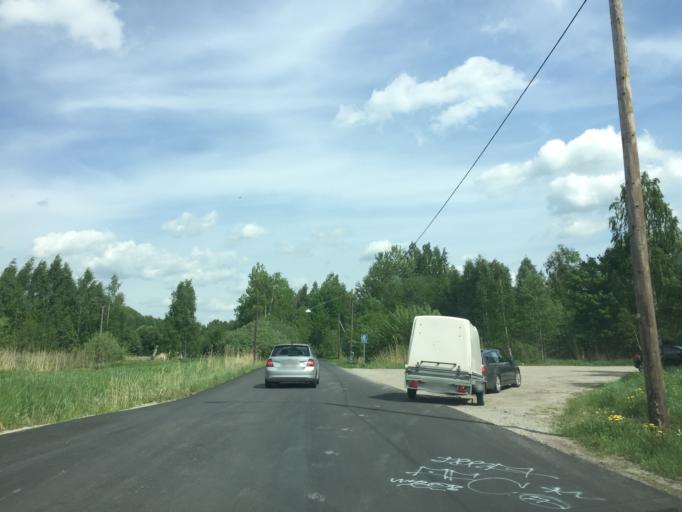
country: SE
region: OErebro
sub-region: Orebro Kommun
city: Orebro
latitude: 59.2772
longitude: 15.2501
